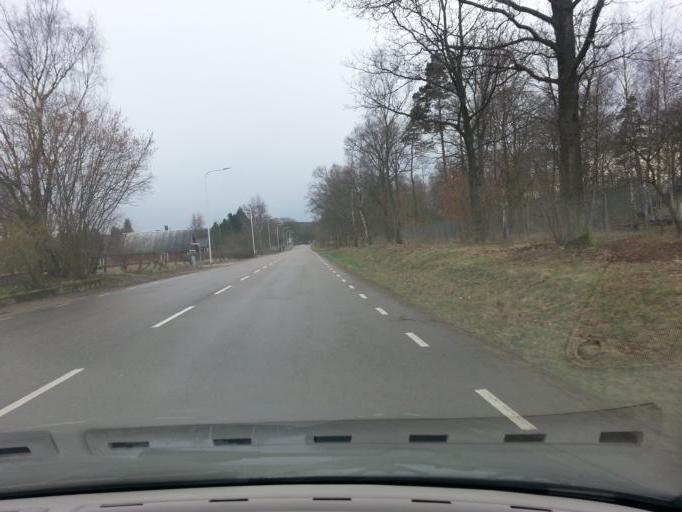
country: SE
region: Skane
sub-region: Klippans Kommun
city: Ljungbyhed
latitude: 56.0709
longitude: 13.2279
